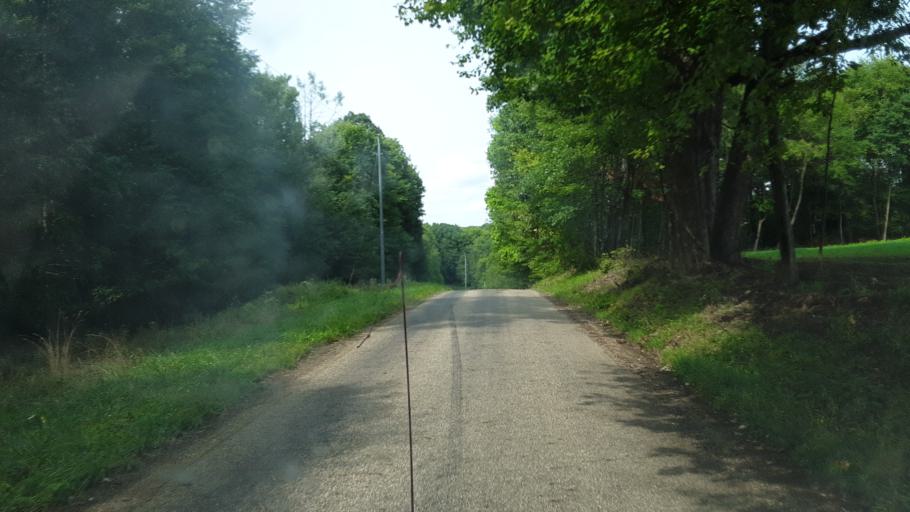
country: US
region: Ohio
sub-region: Ashland County
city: Loudonville
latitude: 40.5739
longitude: -82.3180
